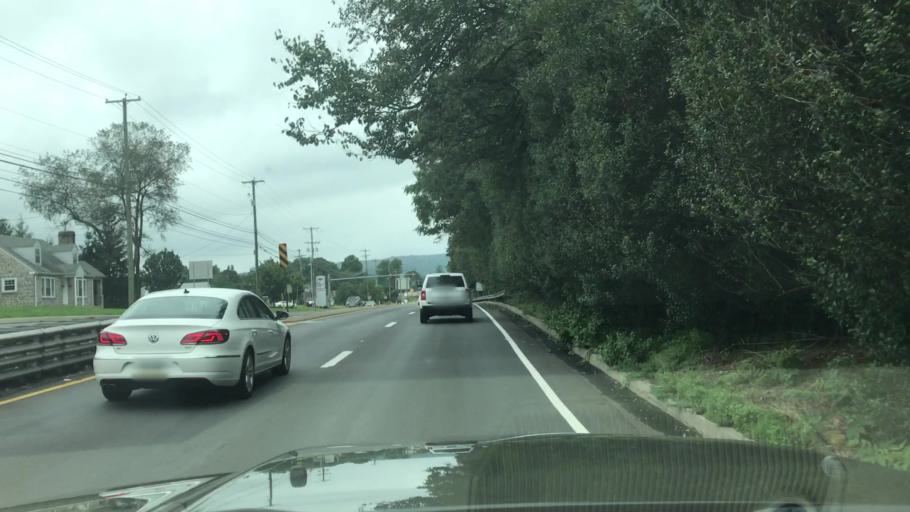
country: US
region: Pennsylvania
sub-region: Berks County
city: Lorane
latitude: 40.3003
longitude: -75.8507
